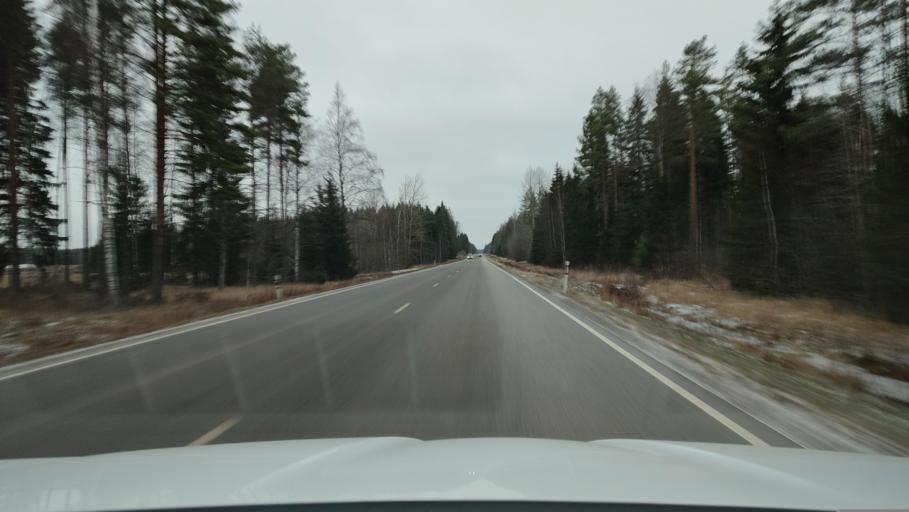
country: FI
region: Ostrobothnia
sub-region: Sydosterbotten
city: Naerpes
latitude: 62.5182
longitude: 21.4566
